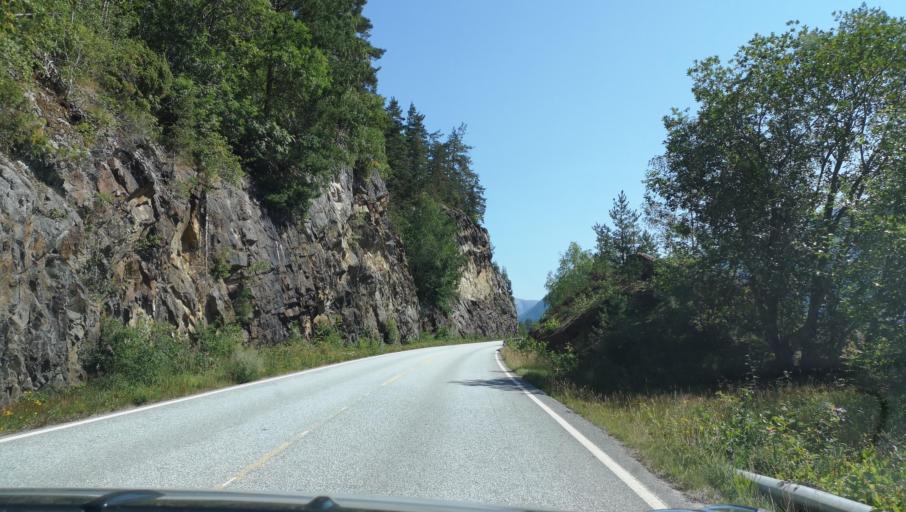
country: NO
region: Hordaland
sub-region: Ulvik
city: Ulvik
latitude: 60.4894
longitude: 6.8432
